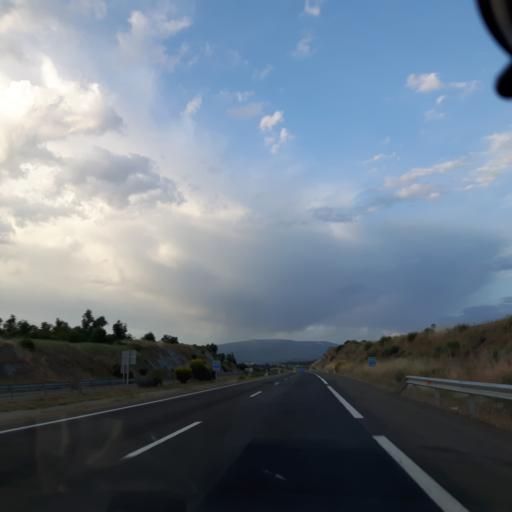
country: ES
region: Castille and Leon
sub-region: Provincia de Salamanca
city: Fuentes de Bejar
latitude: 40.5163
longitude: -5.6734
